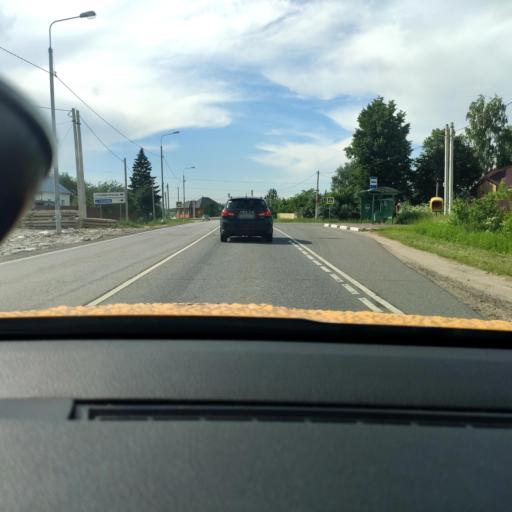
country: RU
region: Moskovskaya
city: Stupino
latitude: 54.9437
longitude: 38.0299
